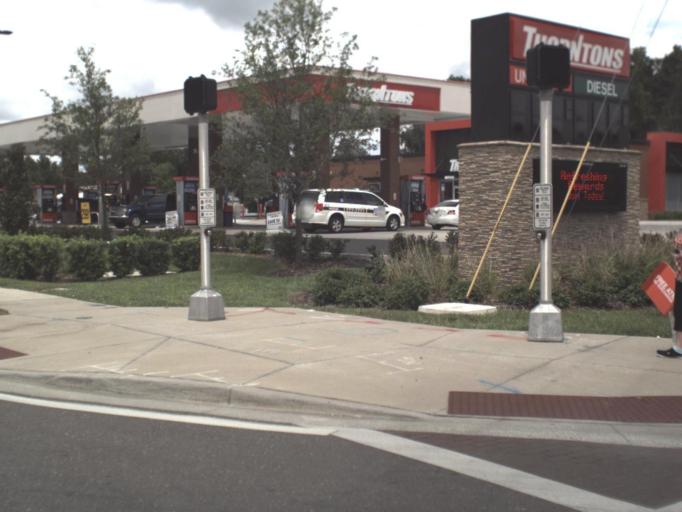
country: US
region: Florida
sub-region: Hillsborough County
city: Town 'n' Country
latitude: 27.9966
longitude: -82.5503
